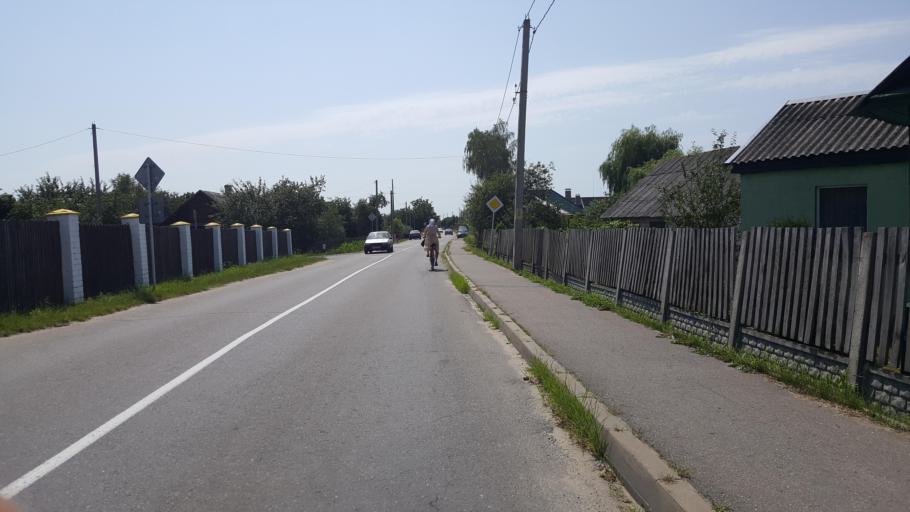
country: BY
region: Brest
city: Zhabinka
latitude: 52.1953
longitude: 24.0115
